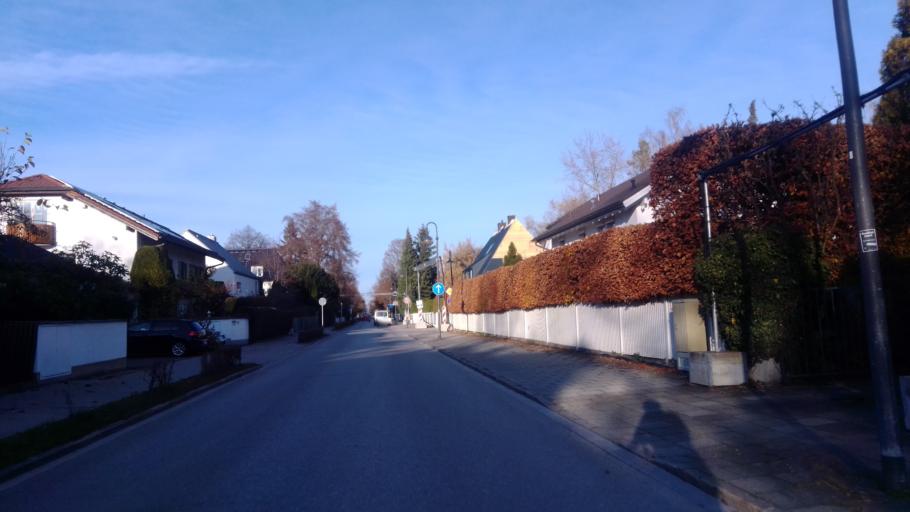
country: DE
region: Bavaria
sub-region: Upper Bavaria
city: Pullach im Isartal
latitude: 48.0689
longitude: 11.5335
